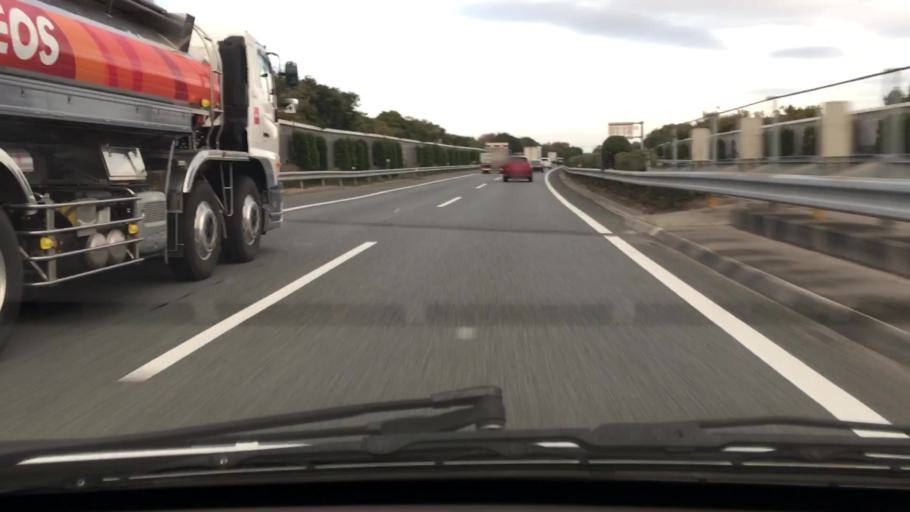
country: JP
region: Chiba
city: Ichihara
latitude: 35.4849
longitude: 140.0824
